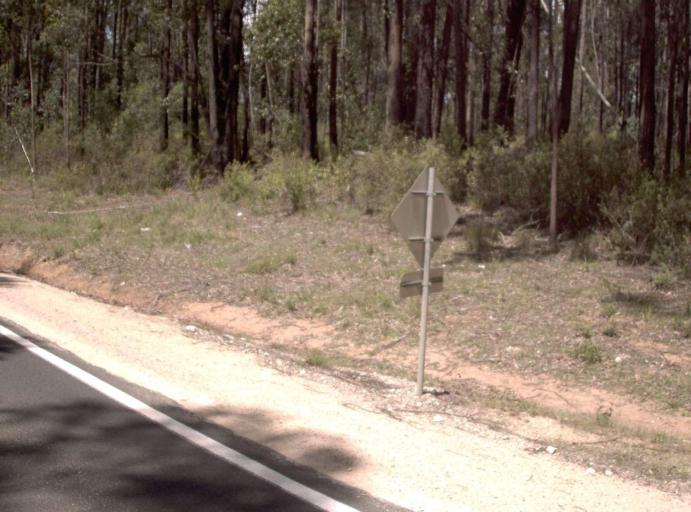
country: AU
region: New South Wales
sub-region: Bombala
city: Bombala
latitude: -37.5742
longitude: 149.0227
